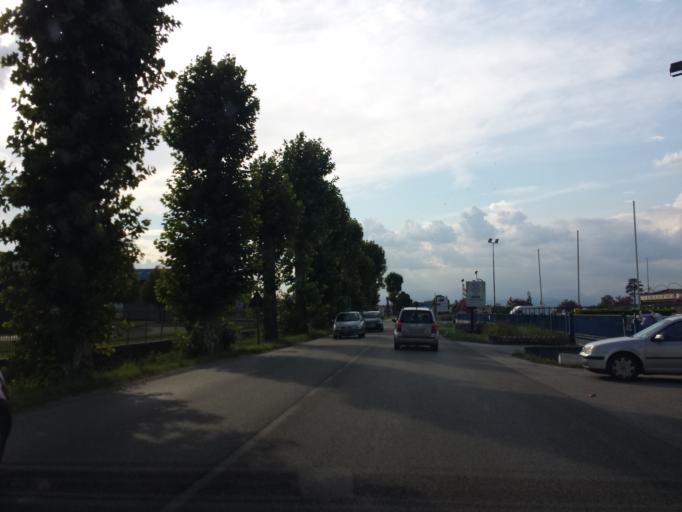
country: IT
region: Veneto
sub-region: Provincia di Vicenza
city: Grumolo delle Abbadesse
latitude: 45.4990
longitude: 11.6501
